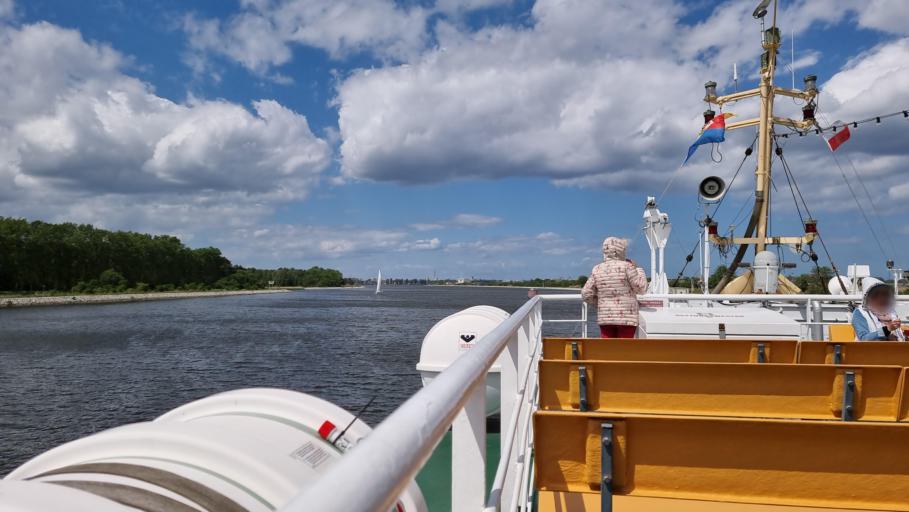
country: PL
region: West Pomeranian Voivodeship
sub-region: Swinoujscie
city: Swinoujscie
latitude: 53.8753
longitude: 14.2742
